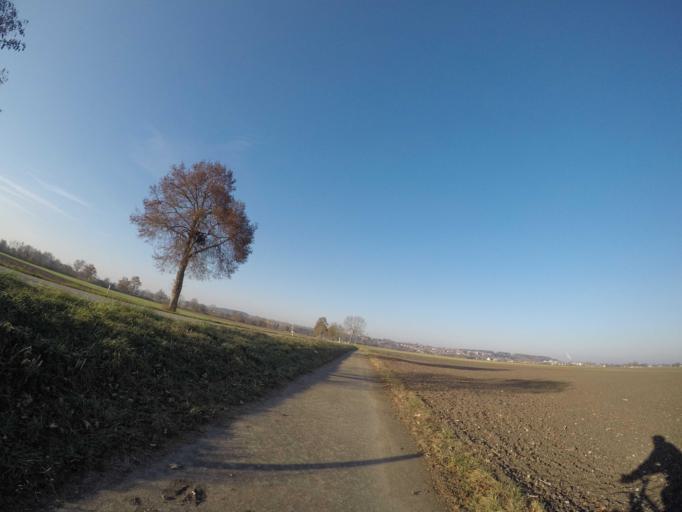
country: DE
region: Baden-Wuerttemberg
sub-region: Tuebingen Region
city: Unterstadion
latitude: 48.2177
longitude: 9.6875
